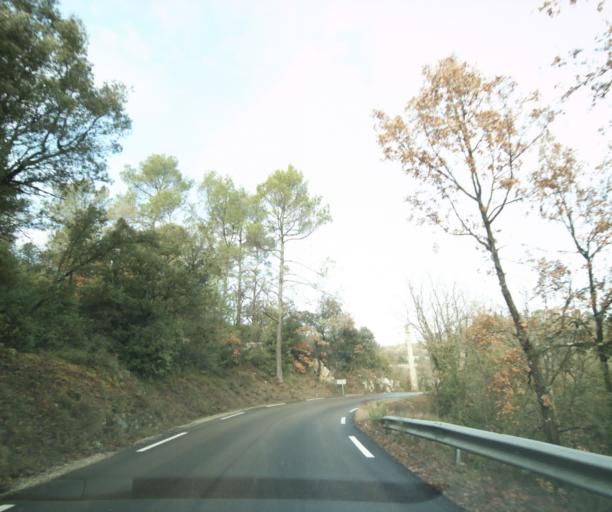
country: FR
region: Provence-Alpes-Cote d'Azur
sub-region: Departement du Var
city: Tourves
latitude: 43.4140
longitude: 5.9257
